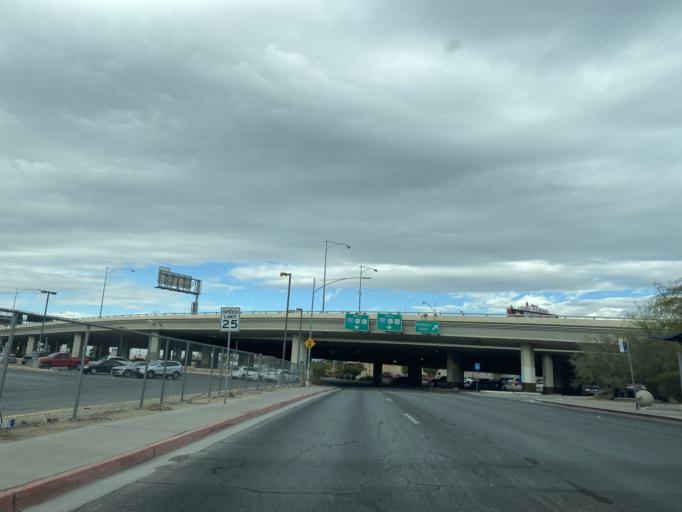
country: US
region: Nevada
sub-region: Clark County
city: Las Vegas
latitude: 36.1734
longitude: -115.1405
